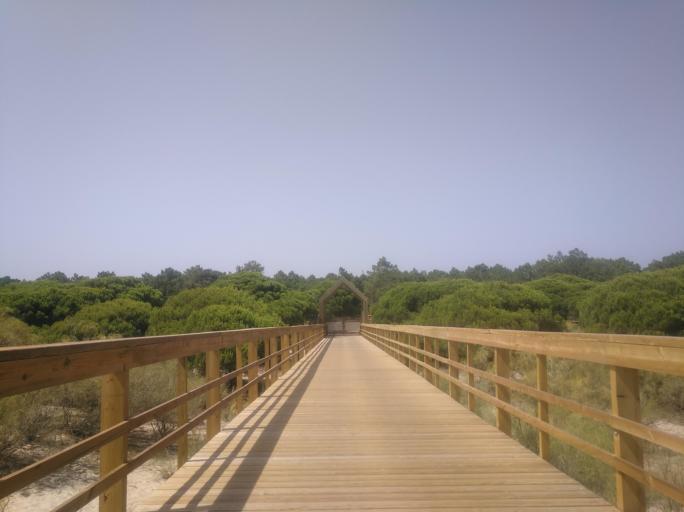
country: PT
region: Faro
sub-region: Vila Real de Santo Antonio
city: Monte Gordo
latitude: 37.1734
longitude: -7.4855
